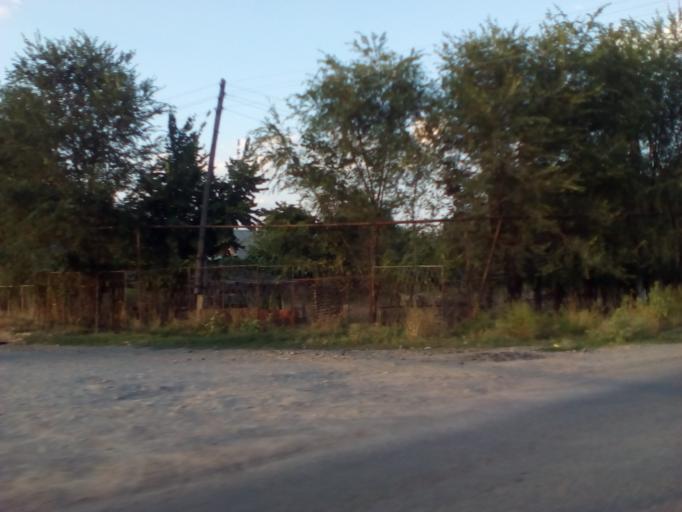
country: KZ
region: Almaty Oblysy
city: Burunday
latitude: 43.1670
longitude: 76.3993
